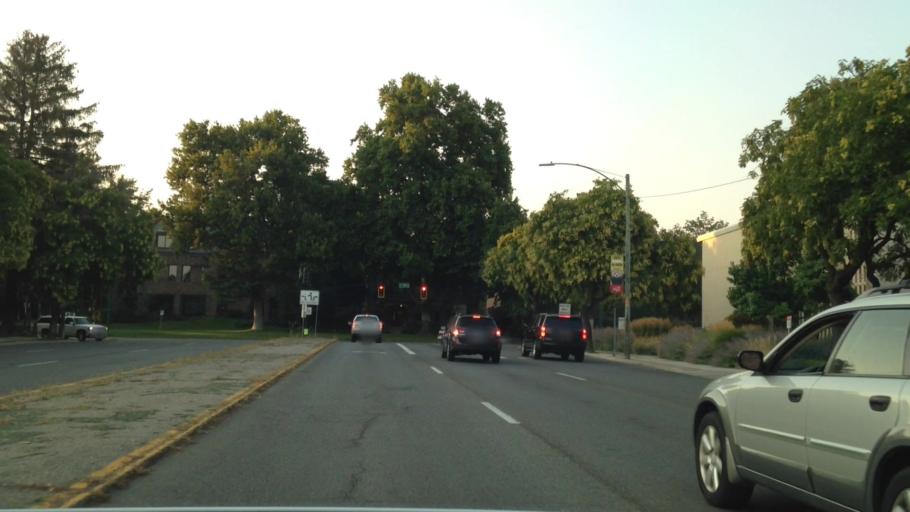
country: US
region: Utah
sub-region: Salt Lake County
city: Salt Lake City
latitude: 40.7685
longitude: -111.8710
